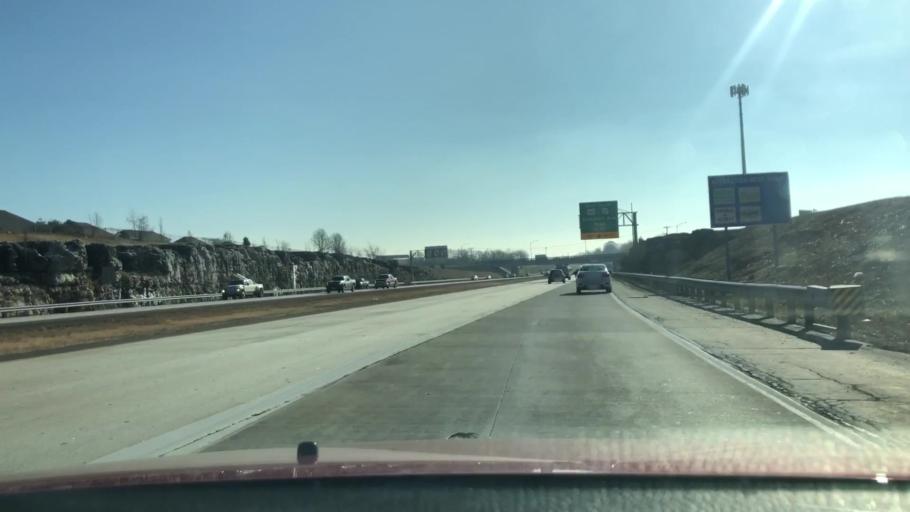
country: US
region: Missouri
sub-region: Greene County
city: Battlefield
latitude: 37.1405
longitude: -93.3146
